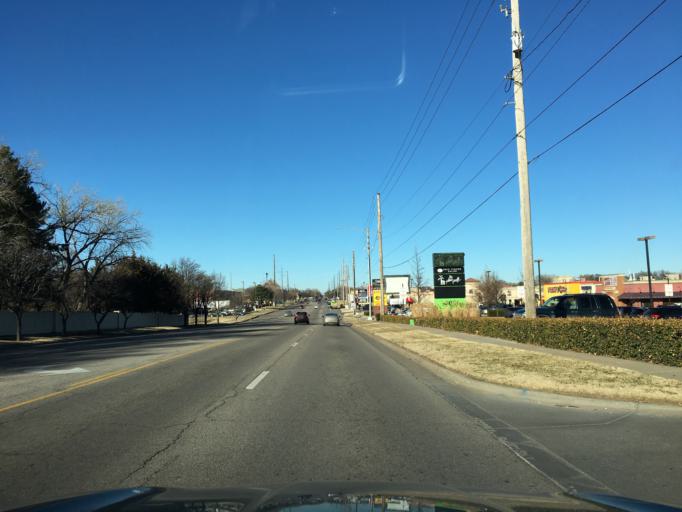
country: US
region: Kansas
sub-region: Sedgwick County
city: Bellaire
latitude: 37.6893
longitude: -97.2444
